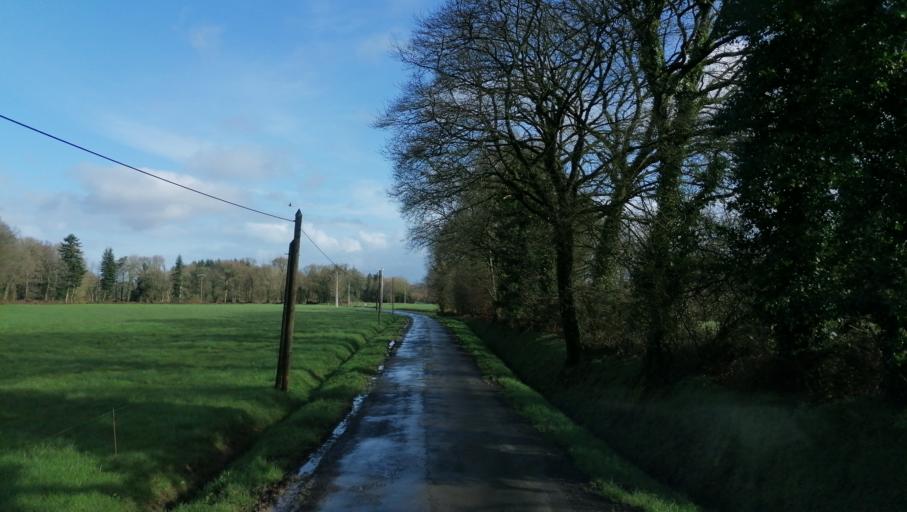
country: FR
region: Brittany
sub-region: Departement des Cotes-d'Armor
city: Lanrodec
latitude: 48.5001
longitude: -3.0152
